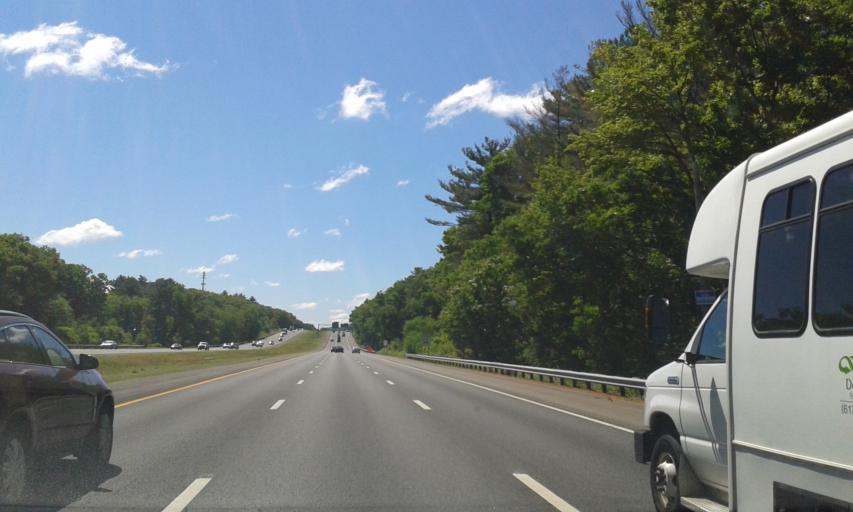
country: US
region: Massachusetts
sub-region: Middlesex County
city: Pinehurst
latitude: 42.4982
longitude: -71.2397
